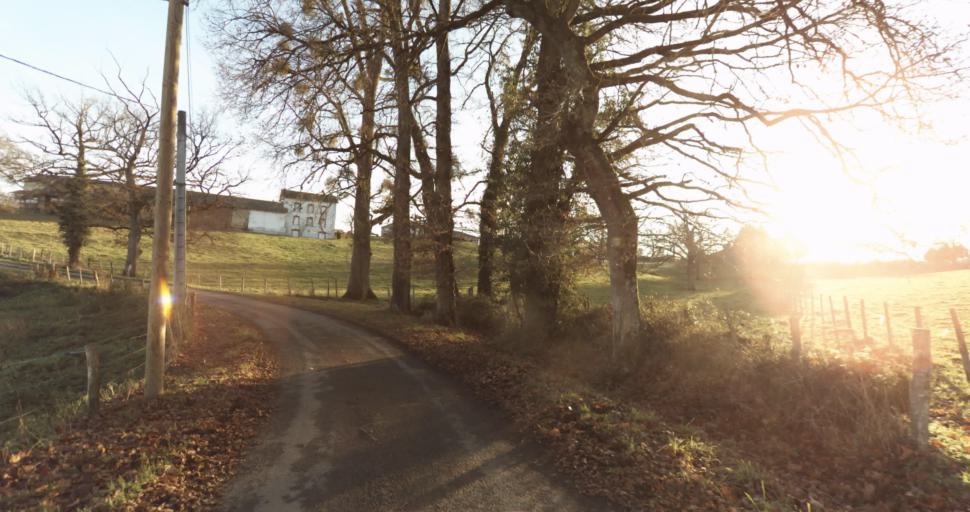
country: FR
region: Limousin
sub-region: Departement de la Haute-Vienne
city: Aixe-sur-Vienne
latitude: 45.7848
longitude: 1.1430
